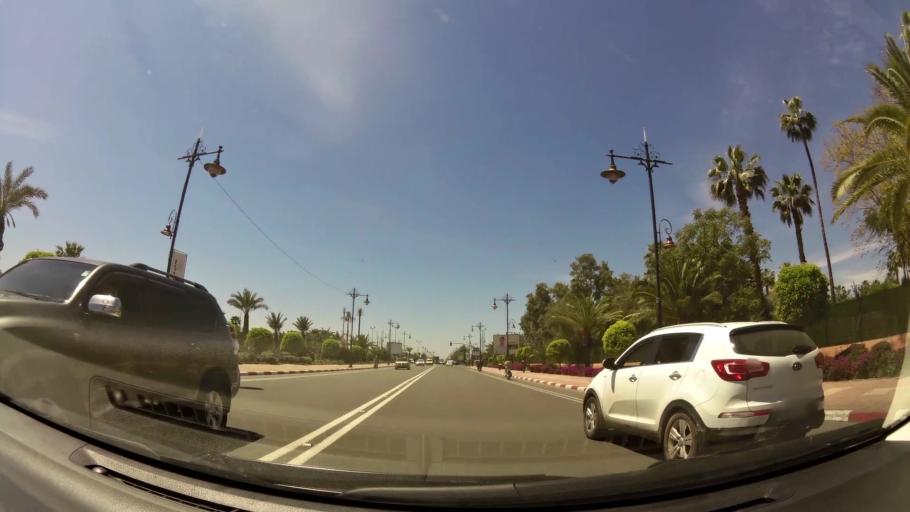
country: MA
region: Marrakech-Tensift-Al Haouz
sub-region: Marrakech
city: Marrakesh
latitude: 31.6182
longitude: -8.0066
